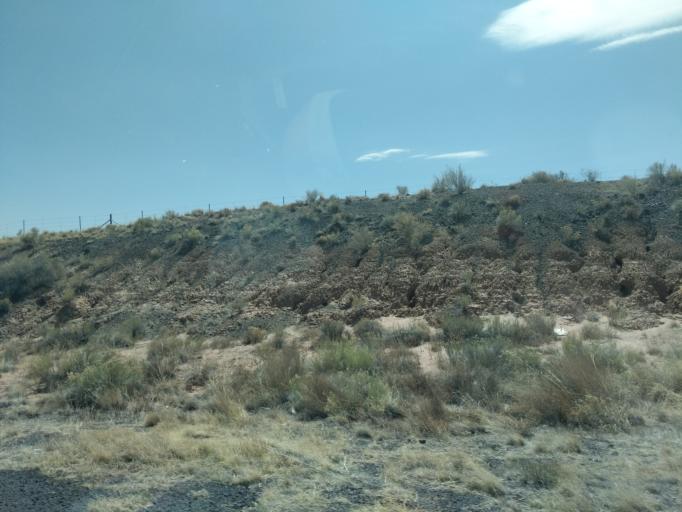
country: US
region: Arizona
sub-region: Navajo County
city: Dilkon
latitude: 35.3956
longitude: -110.0776
